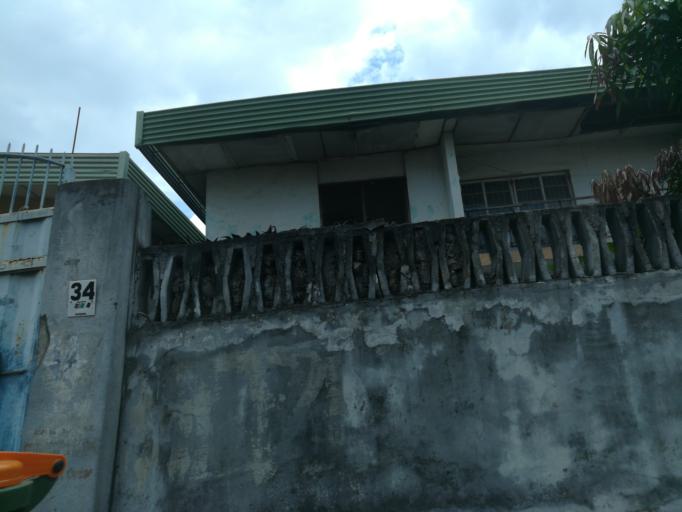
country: NG
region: Lagos
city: Ikeja
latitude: 6.6044
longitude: 3.3496
